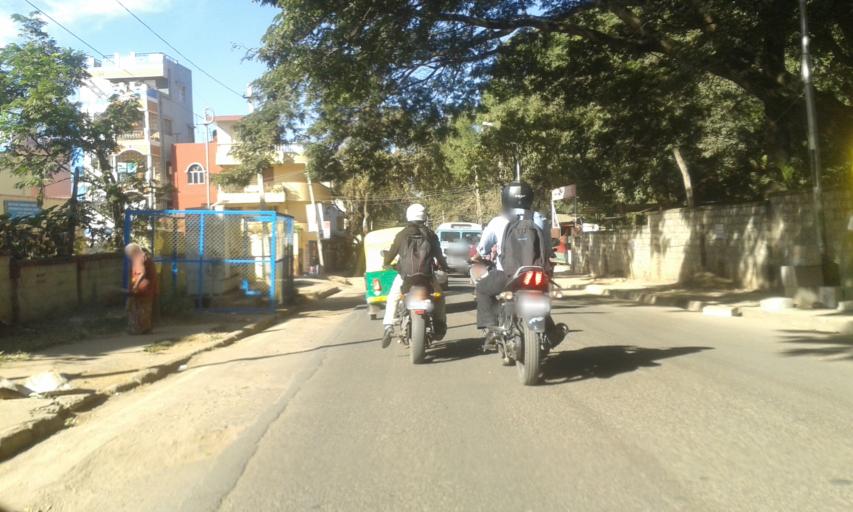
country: IN
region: Karnataka
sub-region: Bangalore Urban
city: Bangalore
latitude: 12.9623
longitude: 77.6182
